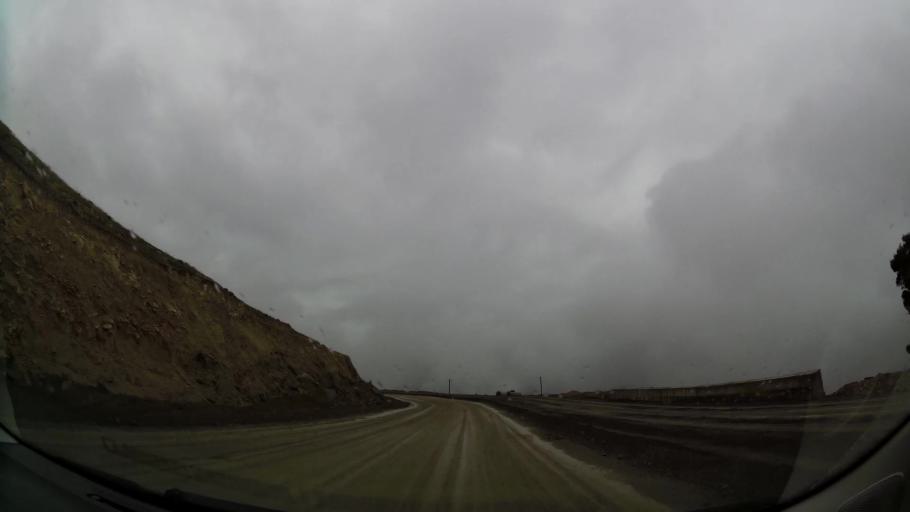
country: MA
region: Taza-Al Hoceima-Taounate
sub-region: Taza
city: Ajdir
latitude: 34.9013
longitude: -3.7863
